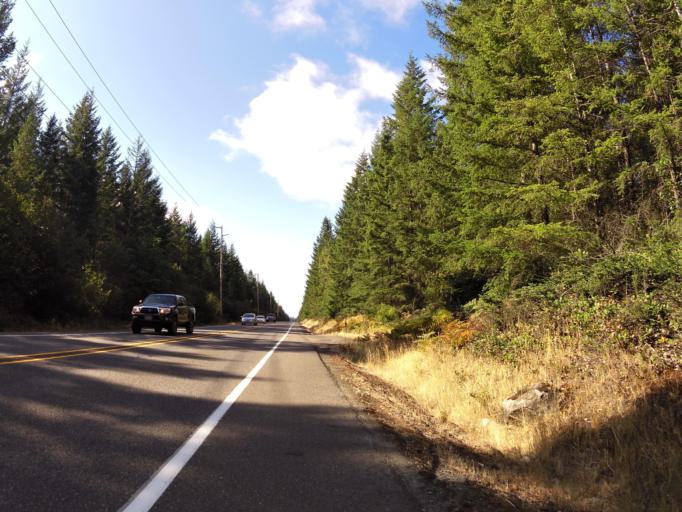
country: US
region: Washington
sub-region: Mason County
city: Allyn
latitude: 47.3071
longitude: -122.9221
